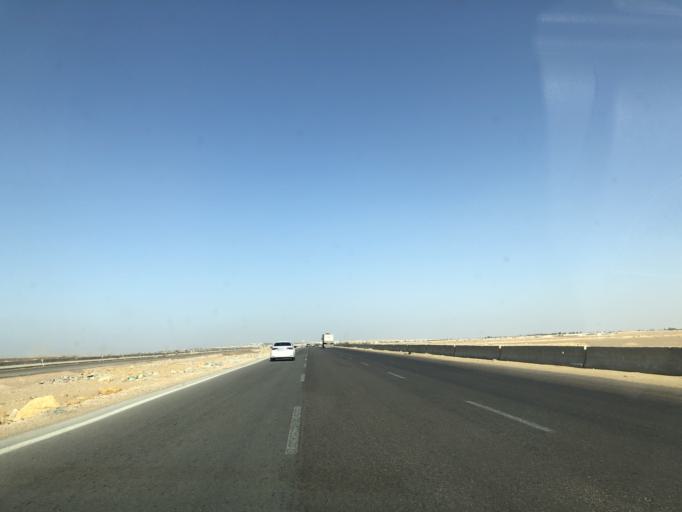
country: EG
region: Muhafazat al Minufiyah
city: Ashmun
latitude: 30.0677
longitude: 30.8875
